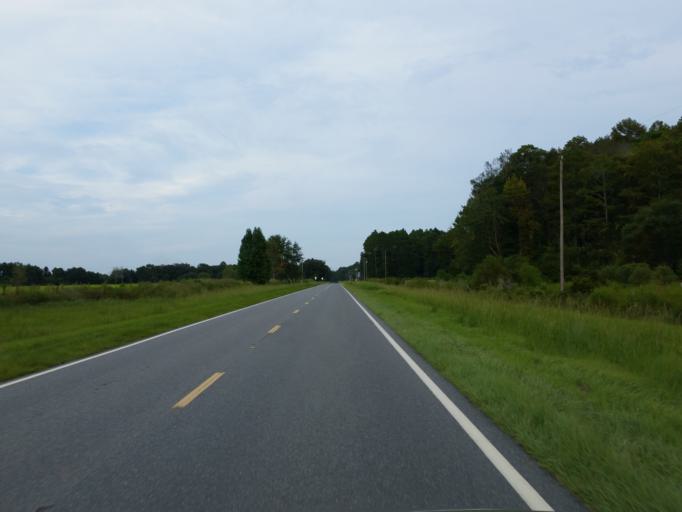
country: US
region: Georgia
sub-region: Echols County
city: Statenville
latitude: 30.5677
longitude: -83.1626
